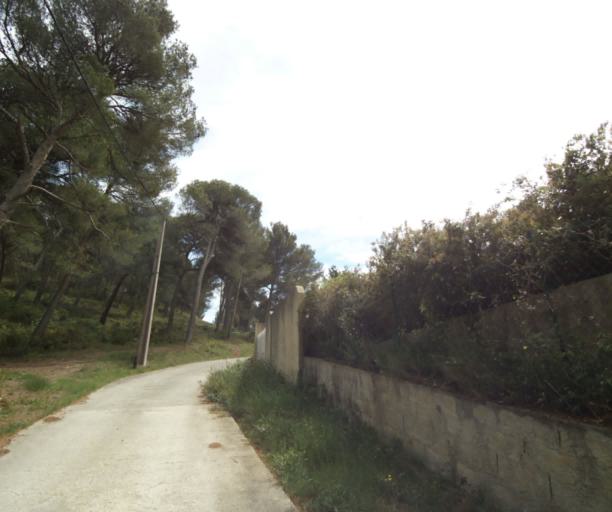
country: FR
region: Provence-Alpes-Cote d'Azur
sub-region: Departement des Bouches-du-Rhone
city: Rognac
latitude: 43.4802
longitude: 5.2434
